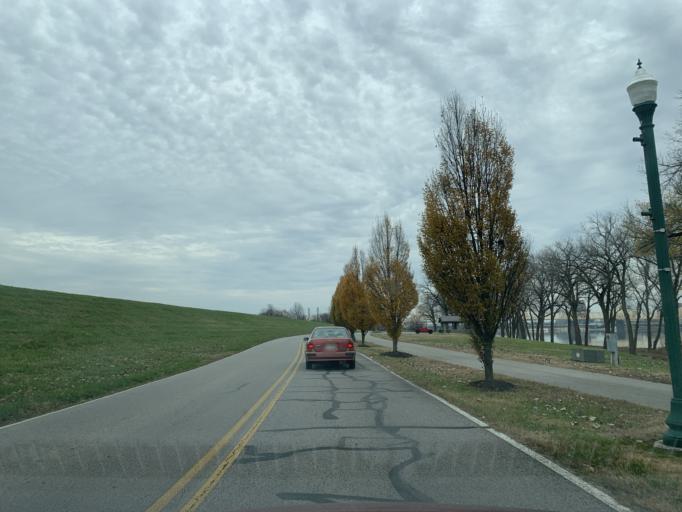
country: US
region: Kentucky
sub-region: Jefferson County
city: Louisville
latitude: 38.2729
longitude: -85.7587
